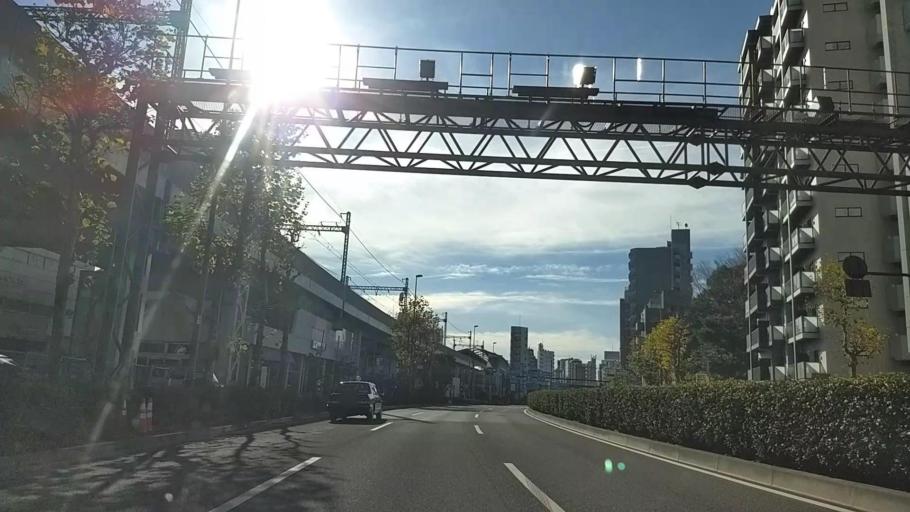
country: JP
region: Tokyo
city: Tokyo
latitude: 35.6194
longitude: 139.7407
